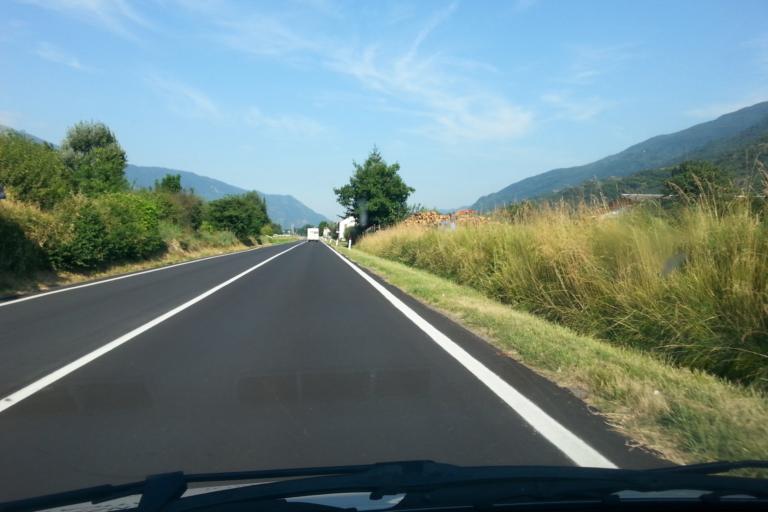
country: IT
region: Piedmont
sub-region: Provincia di Torino
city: Mattie
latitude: 45.1364
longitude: 7.1153
